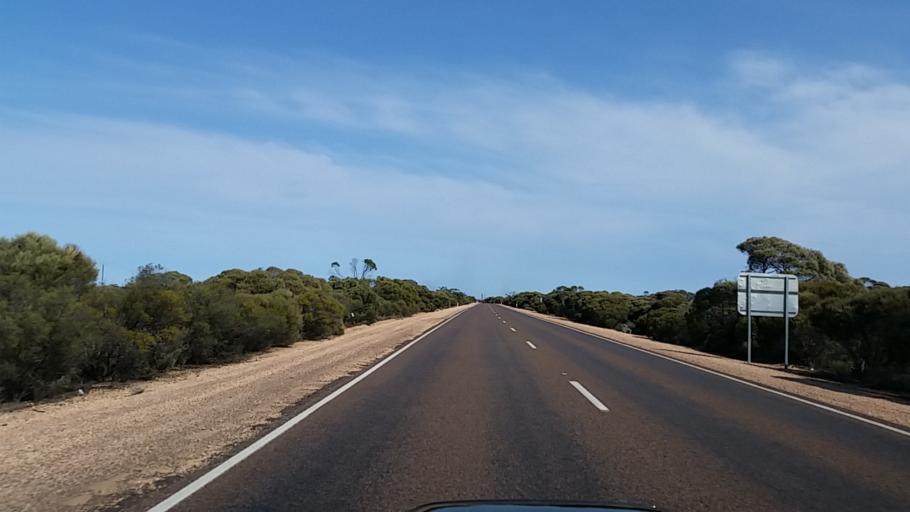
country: AU
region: South Australia
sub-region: Whyalla
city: Whyalla
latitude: -32.9492
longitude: 137.5742
